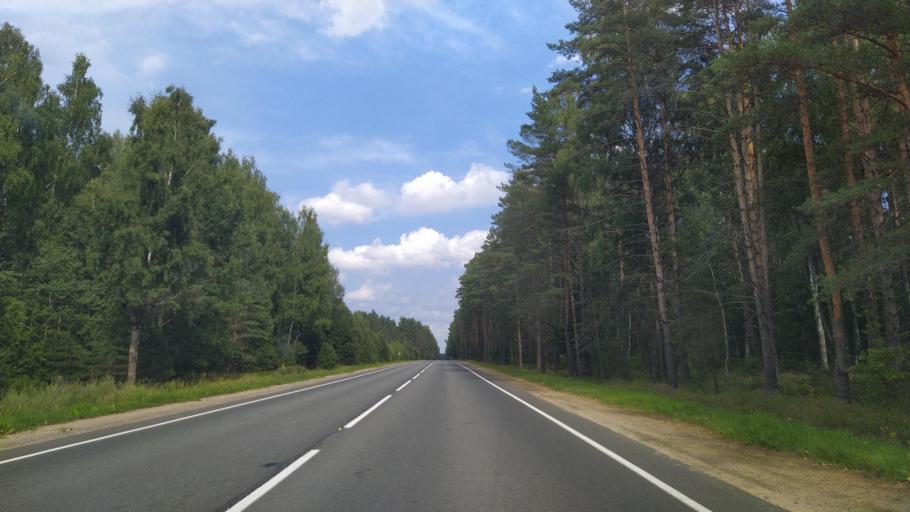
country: RU
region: Pskov
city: Dno
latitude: 57.9837
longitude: 29.7970
